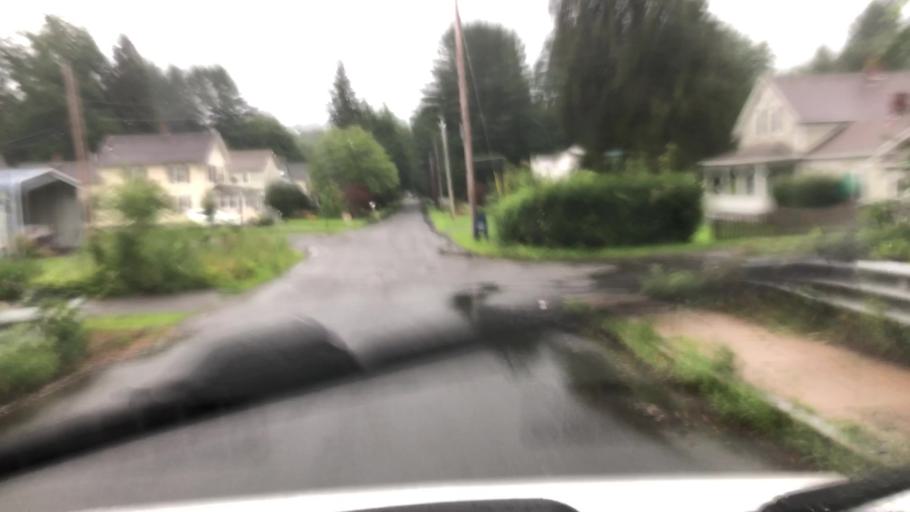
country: US
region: Massachusetts
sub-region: Hampshire County
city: Northampton
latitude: 42.3290
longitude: -72.6752
